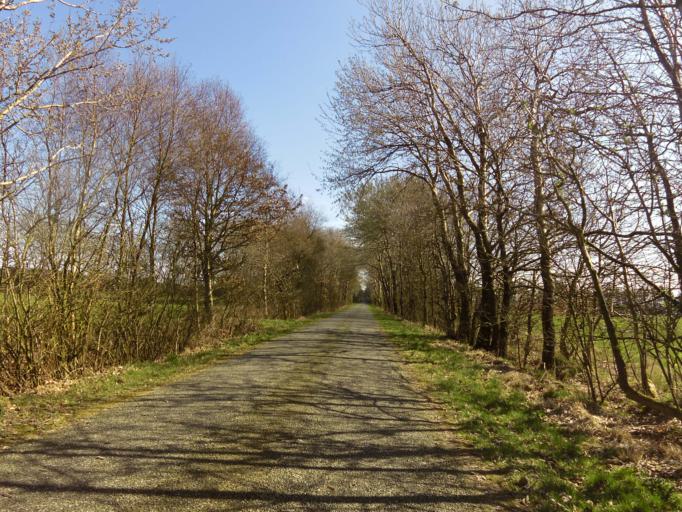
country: DK
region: South Denmark
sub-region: Esbjerg Kommune
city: Ribe
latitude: 55.3452
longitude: 8.8475
